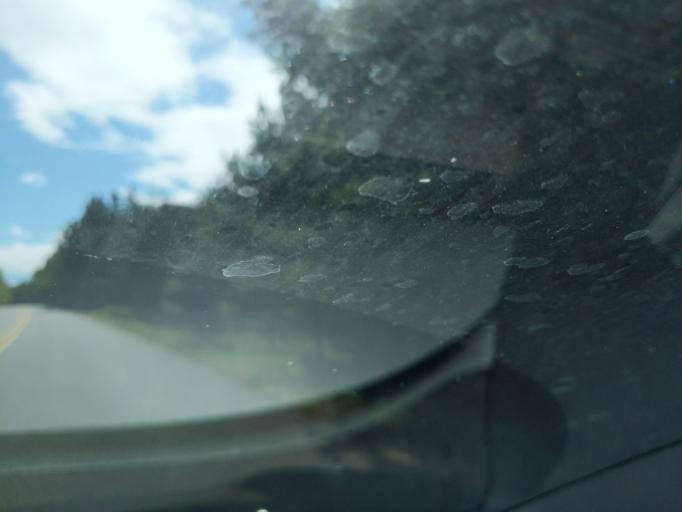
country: US
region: Michigan
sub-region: Antrim County
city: Bellaire
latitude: 45.0617
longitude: -85.3183
